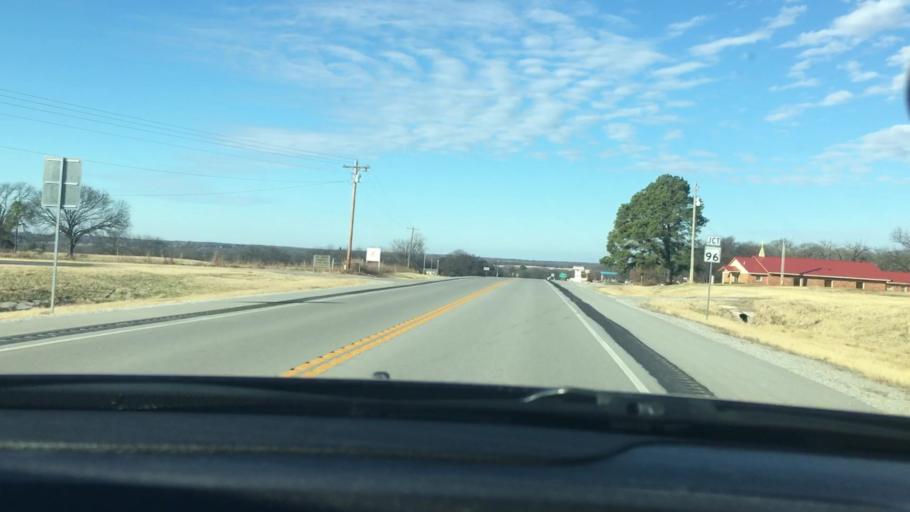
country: US
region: Oklahoma
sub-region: Love County
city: Marietta
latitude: 33.9405
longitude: -97.2772
